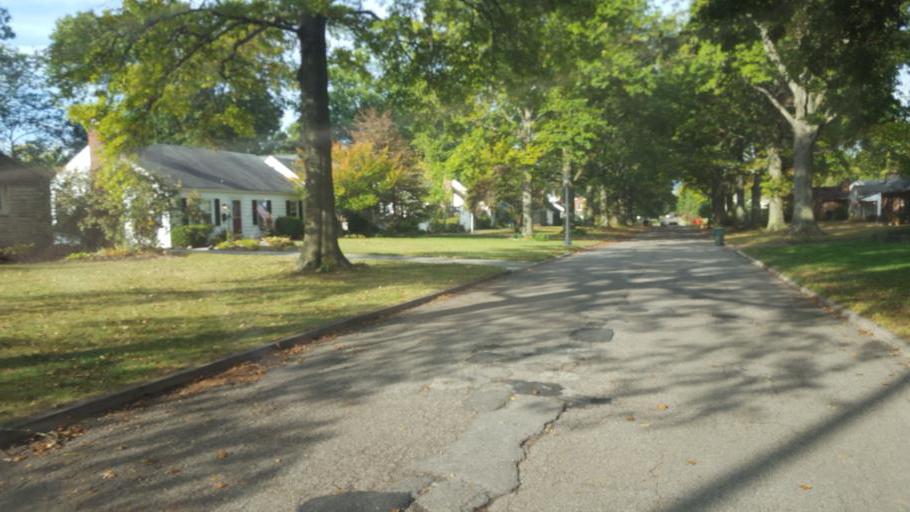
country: US
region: Ohio
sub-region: Franklin County
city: Worthington
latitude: 40.0405
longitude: -83.0048
